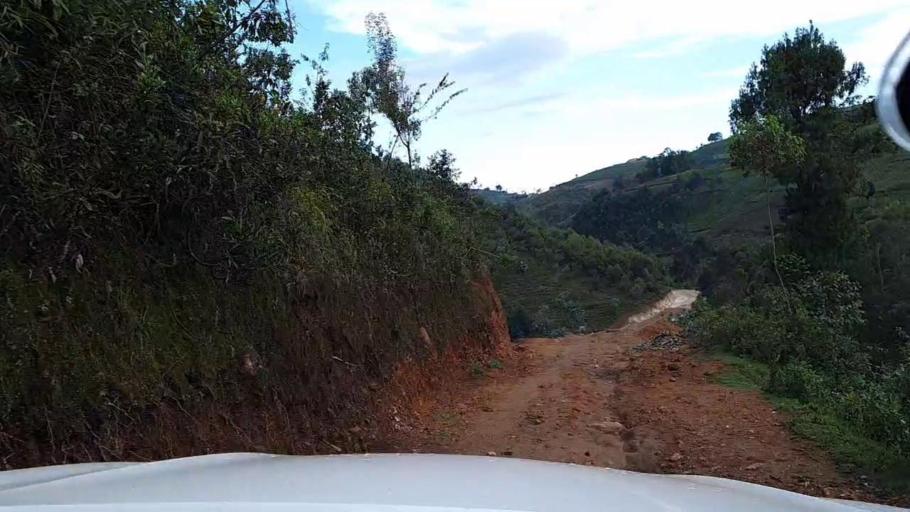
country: BI
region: Kayanza
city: Kayanza
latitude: -2.7793
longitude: 29.4498
